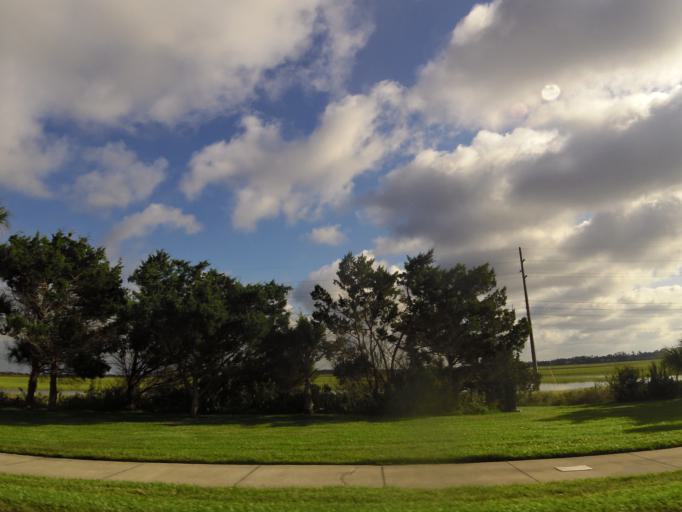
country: US
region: Georgia
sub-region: Glynn County
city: Saint Simons Island
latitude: 31.1816
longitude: -81.3652
